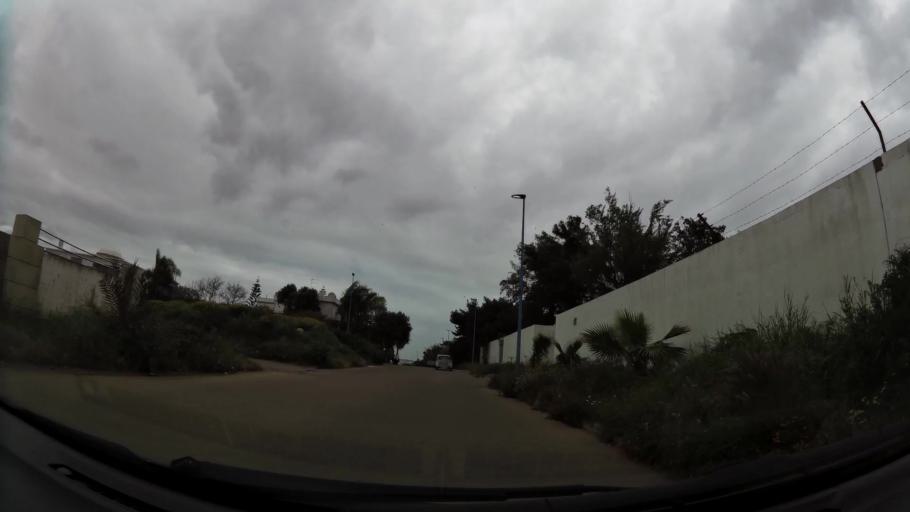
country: MA
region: Grand Casablanca
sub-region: Casablanca
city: Casablanca
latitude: 33.5359
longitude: -7.6361
